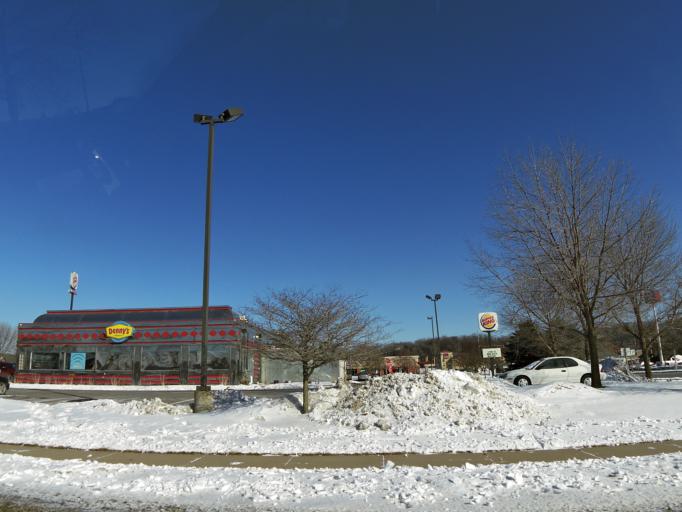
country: US
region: Wisconsin
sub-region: Saint Croix County
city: Hudson
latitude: 44.9586
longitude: -92.7232
